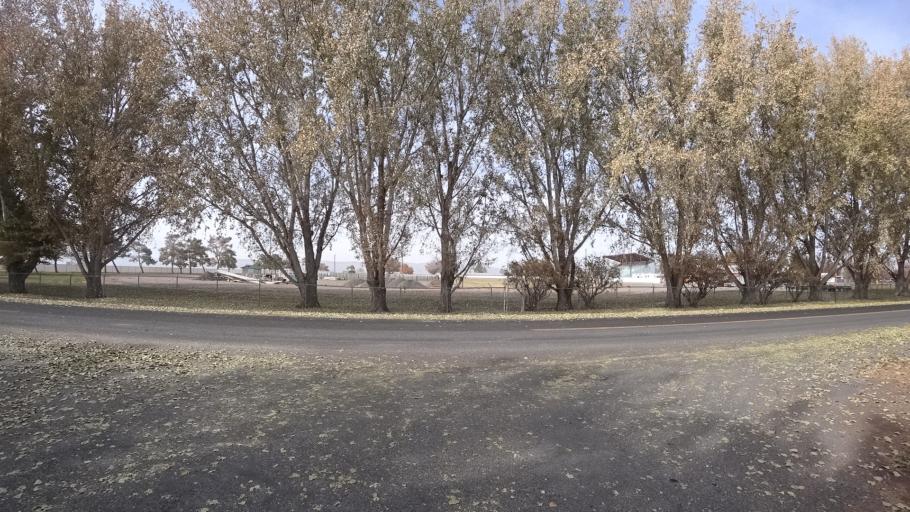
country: US
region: California
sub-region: Siskiyou County
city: Tulelake
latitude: 41.9481
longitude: -121.4765
